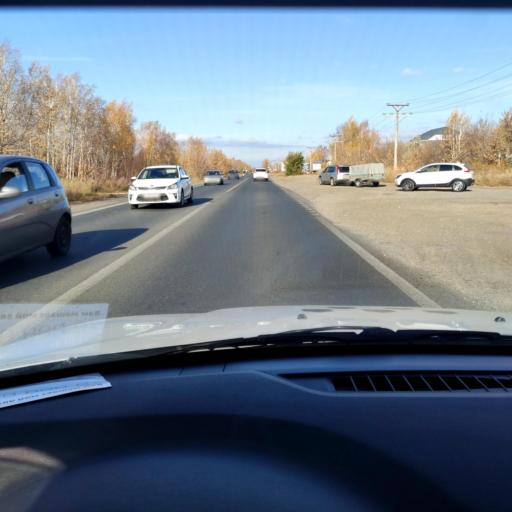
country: RU
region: Samara
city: Tol'yatti
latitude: 53.5516
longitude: 49.3711
